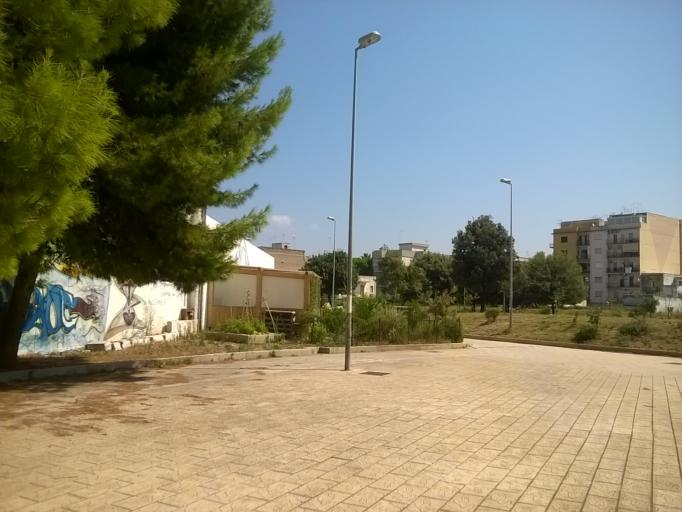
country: IT
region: Apulia
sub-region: Provincia di Taranto
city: Taranto
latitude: 40.4639
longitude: 17.2747
